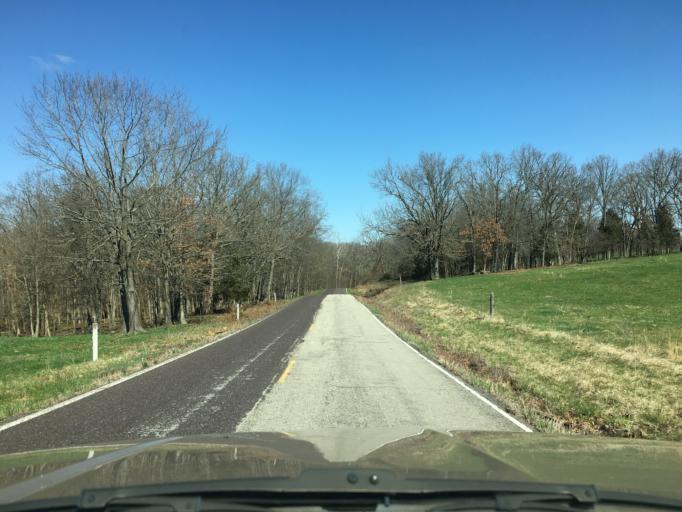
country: US
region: Missouri
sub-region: Franklin County
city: New Haven
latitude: 38.5401
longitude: -91.3292
